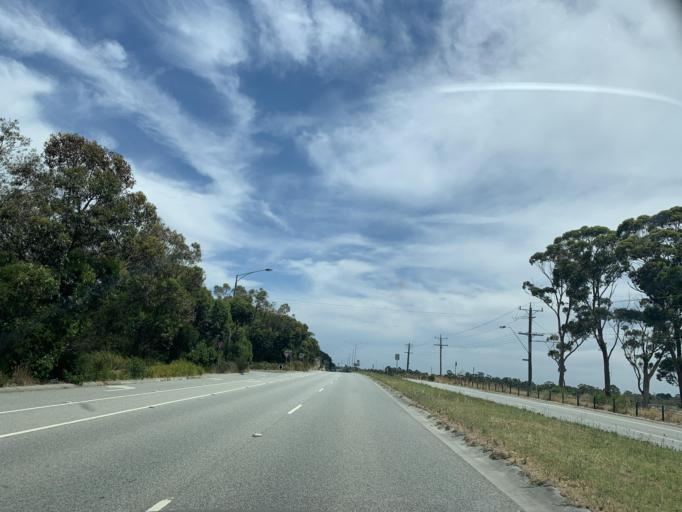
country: AU
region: Victoria
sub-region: Casey
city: Cranbourne South
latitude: -38.1295
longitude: 145.2380
